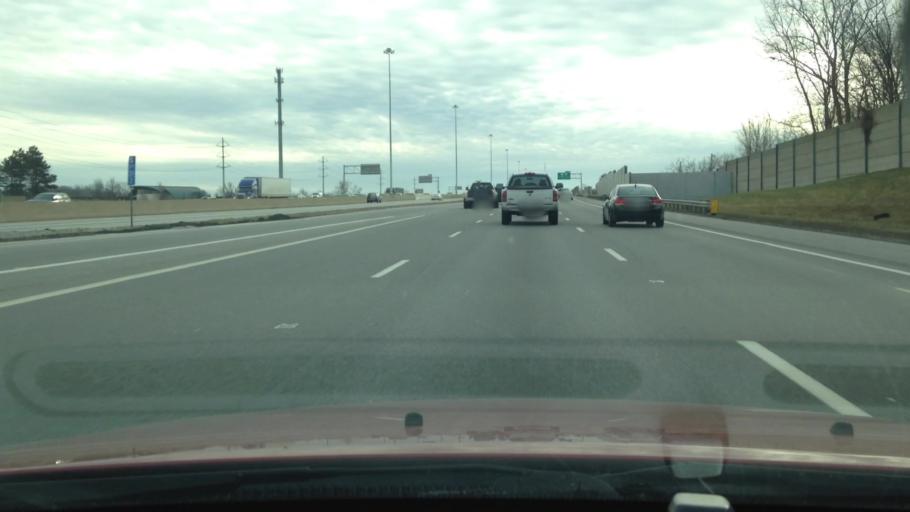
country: US
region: Ohio
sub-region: Cuyahoga County
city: Pepper Pike
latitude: 41.4818
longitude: -81.4873
